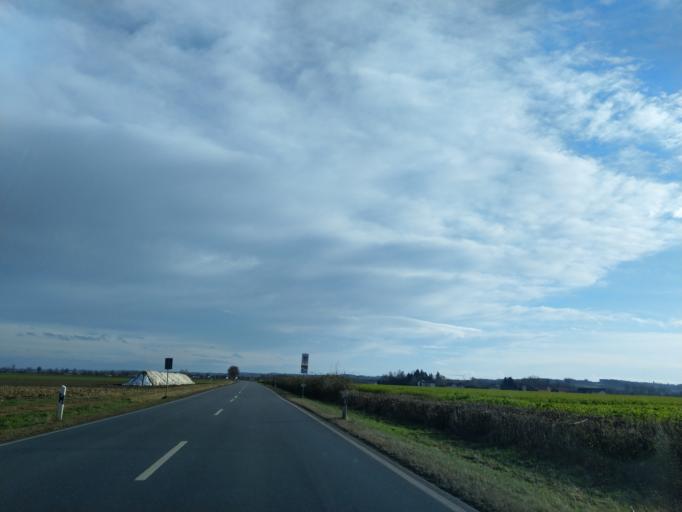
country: DE
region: Bavaria
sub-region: Lower Bavaria
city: Aldersbach
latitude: 48.6141
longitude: 13.0202
